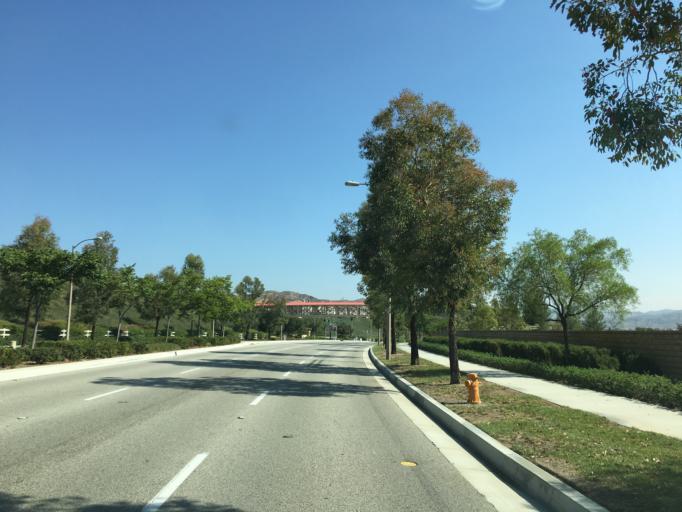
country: US
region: California
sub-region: Los Angeles County
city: Valencia
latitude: 34.4564
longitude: -118.5664
